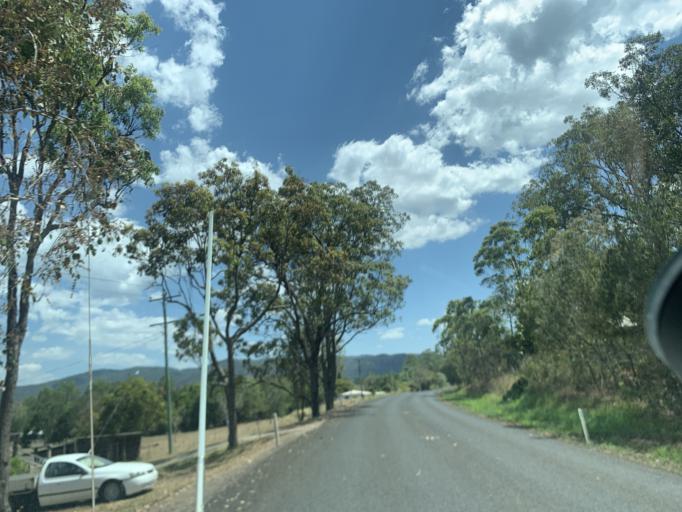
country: AU
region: Queensland
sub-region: Tablelands
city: Atherton
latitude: -17.2997
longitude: 145.4720
